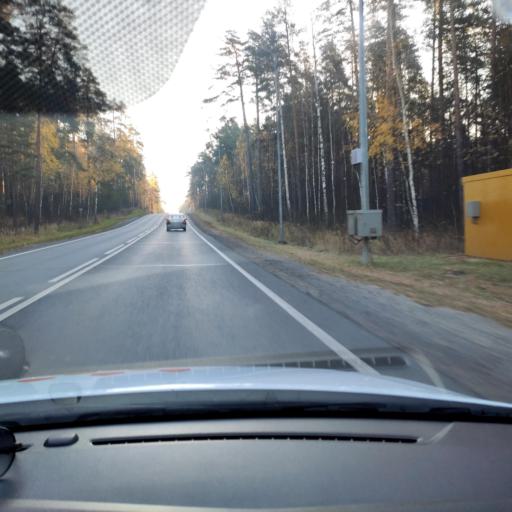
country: RU
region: Tatarstan
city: Stolbishchi
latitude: 55.6343
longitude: 49.0873
